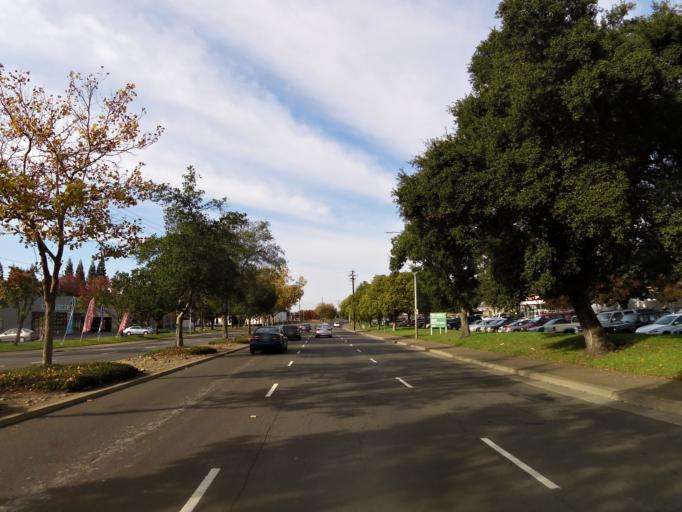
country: US
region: California
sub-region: Sacramento County
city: Rancho Cordova
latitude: 38.5772
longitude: -121.2608
